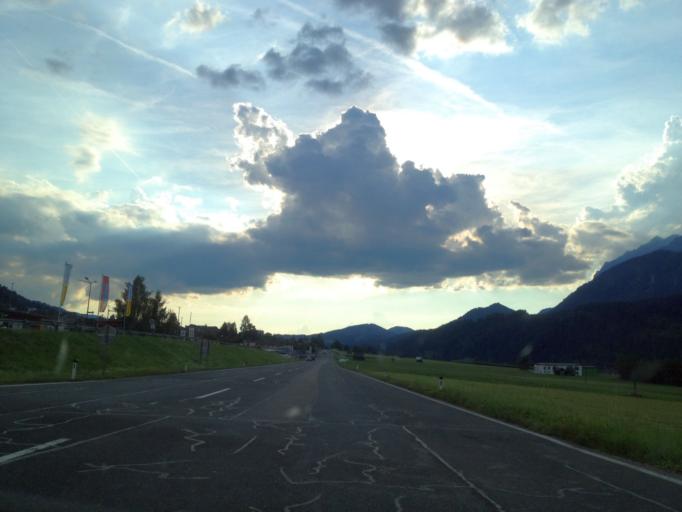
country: AT
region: Styria
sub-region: Politischer Bezirk Liezen
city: Haus im Ennstal
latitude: 47.4120
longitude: 13.7798
